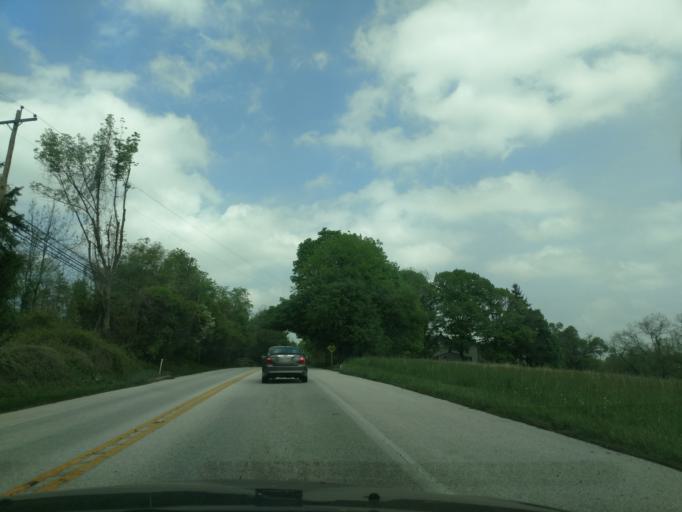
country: US
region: Pennsylvania
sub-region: Montgomery County
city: Stowe
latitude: 40.1752
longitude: -75.7153
